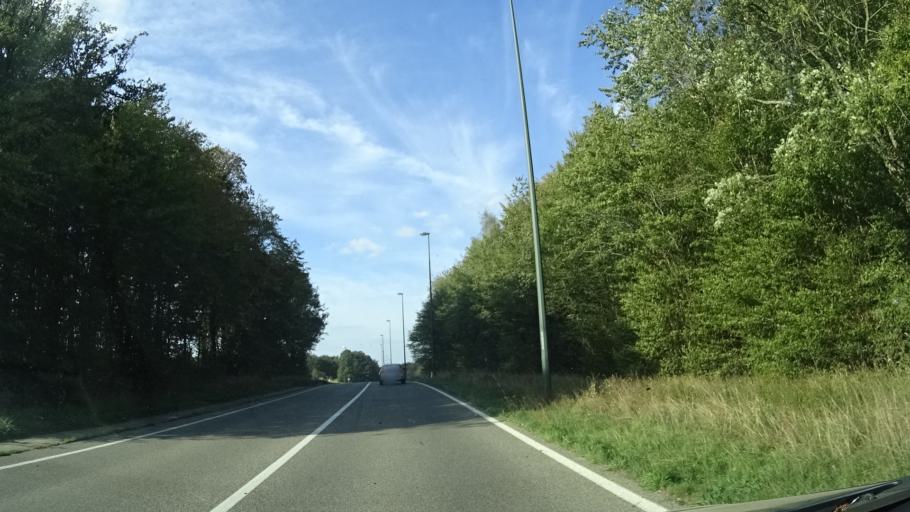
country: BE
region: Wallonia
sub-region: Province de Namur
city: Cerfontaine
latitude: 50.2103
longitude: 4.3812
